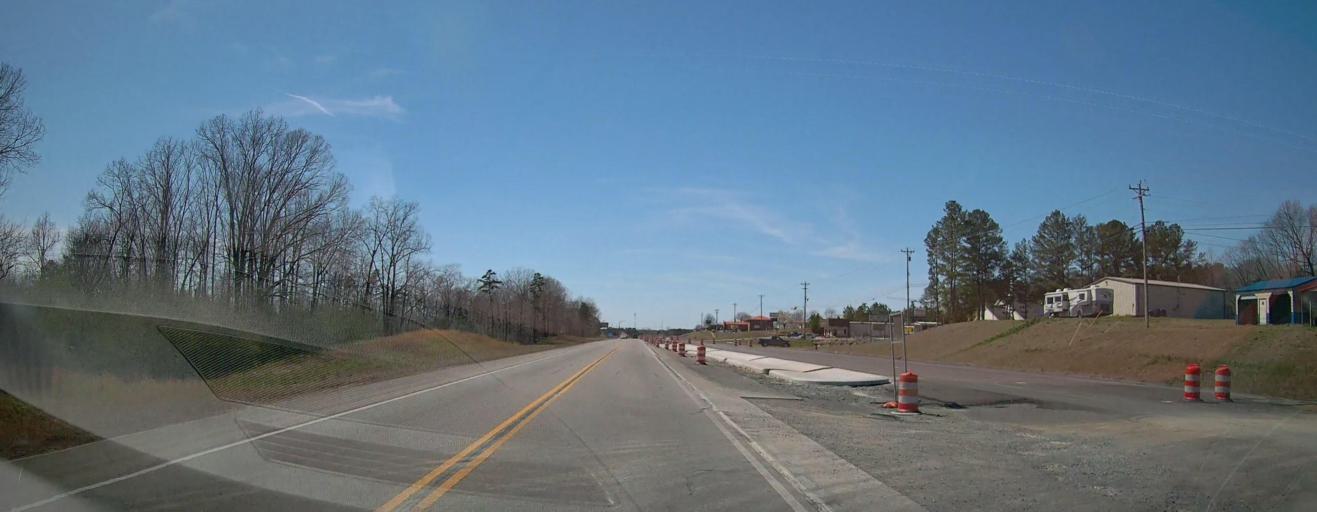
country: US
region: Alabama
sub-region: Cullman County
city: Cullman
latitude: 34.1989
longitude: -86.7975
